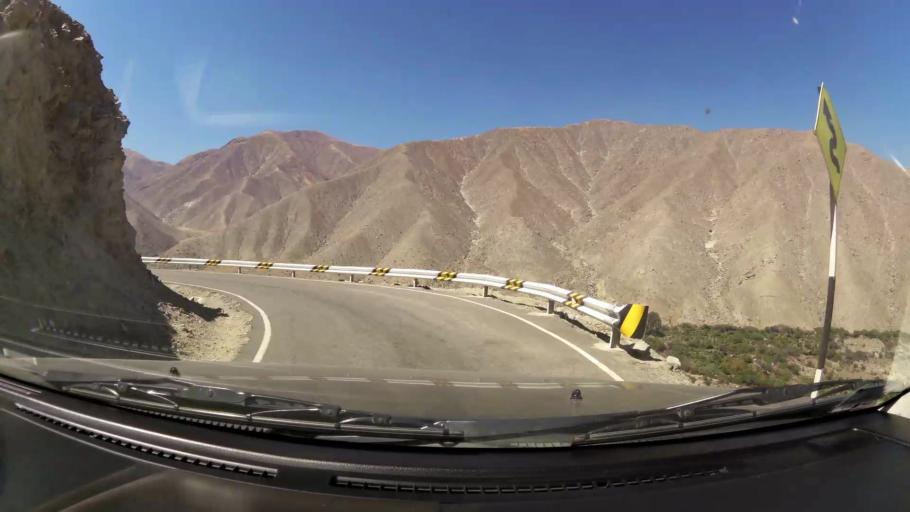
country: PE
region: Ica
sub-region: Provincia de Pisco
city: Huancano
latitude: -13.8374
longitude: -75.5551
